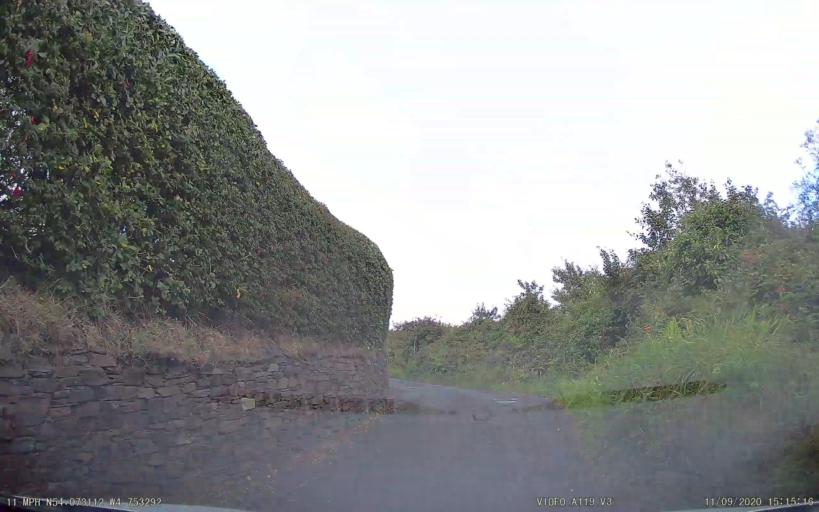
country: IM
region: Port Erin
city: Port Erin
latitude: 54.0731
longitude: -4.7533
